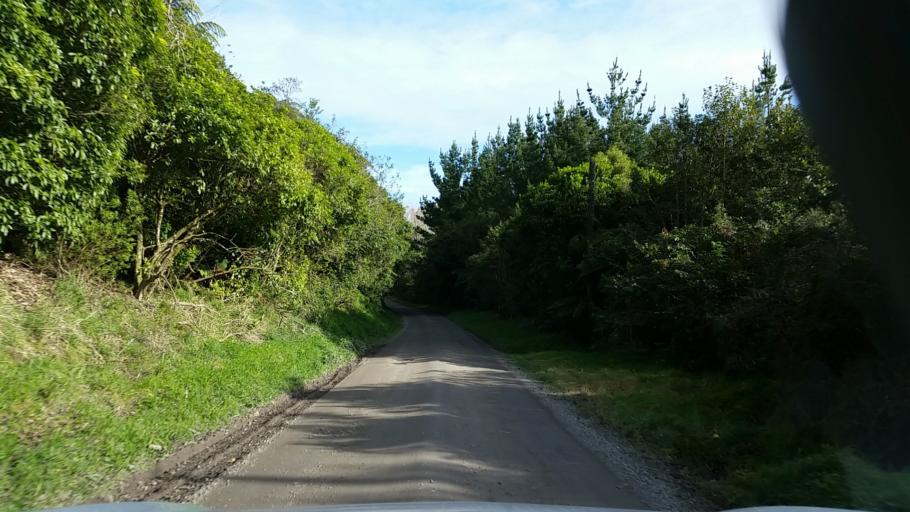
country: NZ
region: Bay of Plenty
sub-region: Rotorua District
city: Rotorua
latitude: -38.2384
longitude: 176.3535
